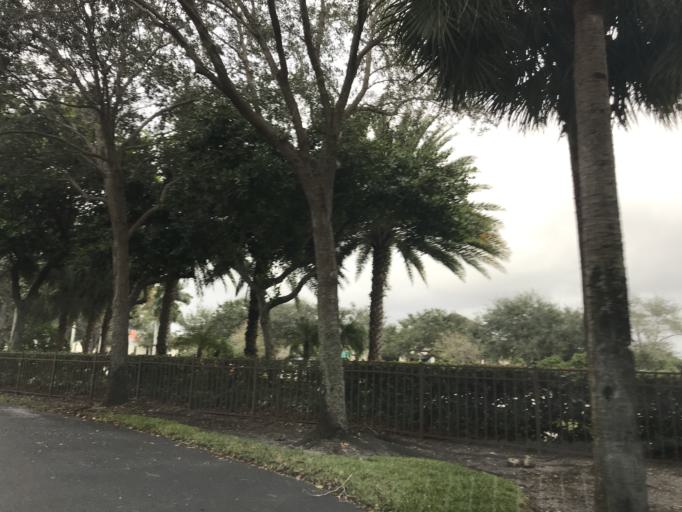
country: US
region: Florida
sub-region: Broward County
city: Coral Springs
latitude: 26.2976
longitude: -80.2794
